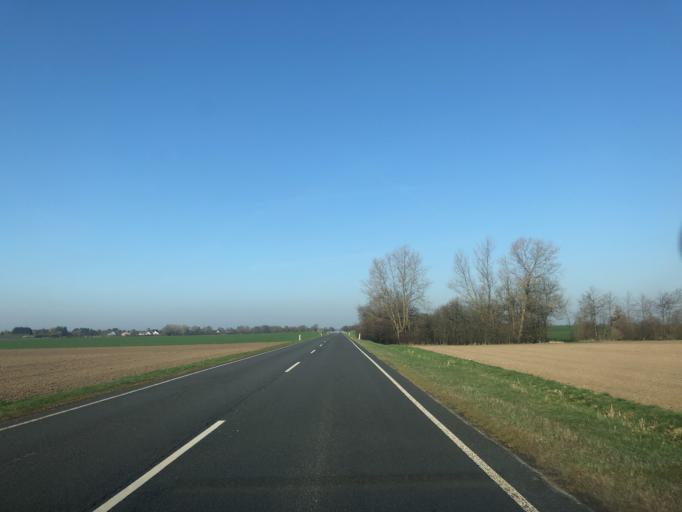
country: DK
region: Zealand
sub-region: Stevns Kommune
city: Harlev
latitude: 55.2798
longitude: 12.2772
